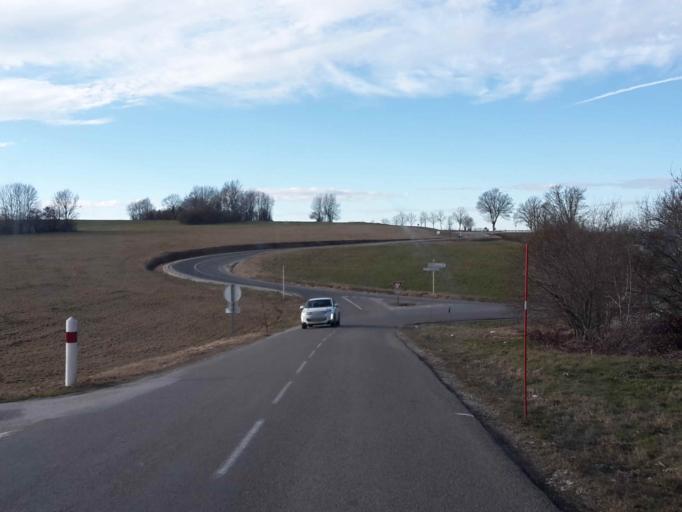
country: FR
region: Franche-Comte
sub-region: Departement du Doubs
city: Valdahon
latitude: 47.1413
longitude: 6.3729
